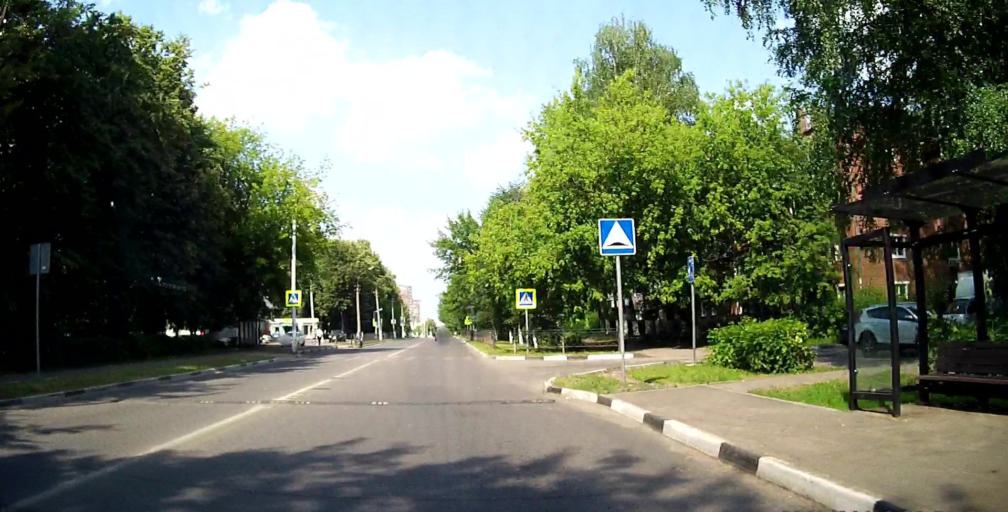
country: RU
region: Moskovskaya
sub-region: Podol'skiy Rayon
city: Podol'sk
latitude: 55.4165
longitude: 37.5312
